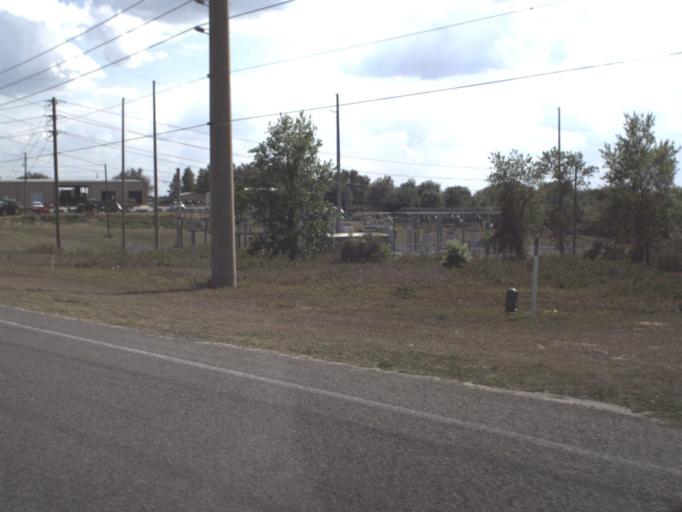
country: US
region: Florida
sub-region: Lake County
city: Minneola
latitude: 28.5992
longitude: -81.7545
